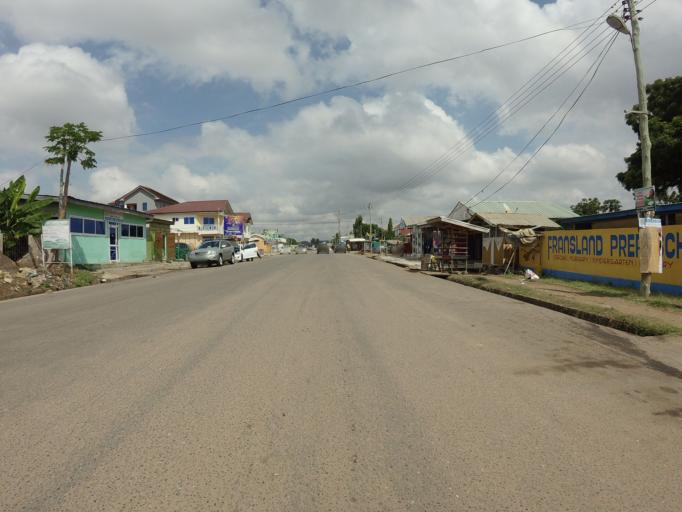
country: GH
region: Greater Accra
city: Nungua
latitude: 5.6133
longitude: -0.0829
